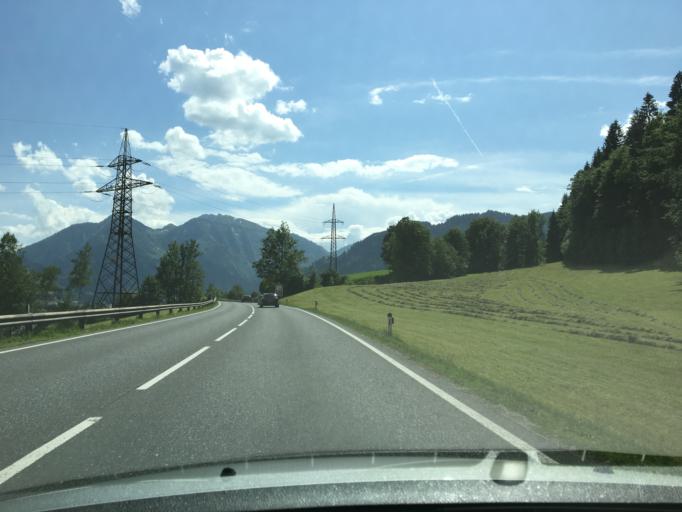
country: AT
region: Salzburg
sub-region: Politischer Bezirk Sankt Johann im Pongau
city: Sankt Johann im Pongau
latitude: 47.3661
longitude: 13.2035
